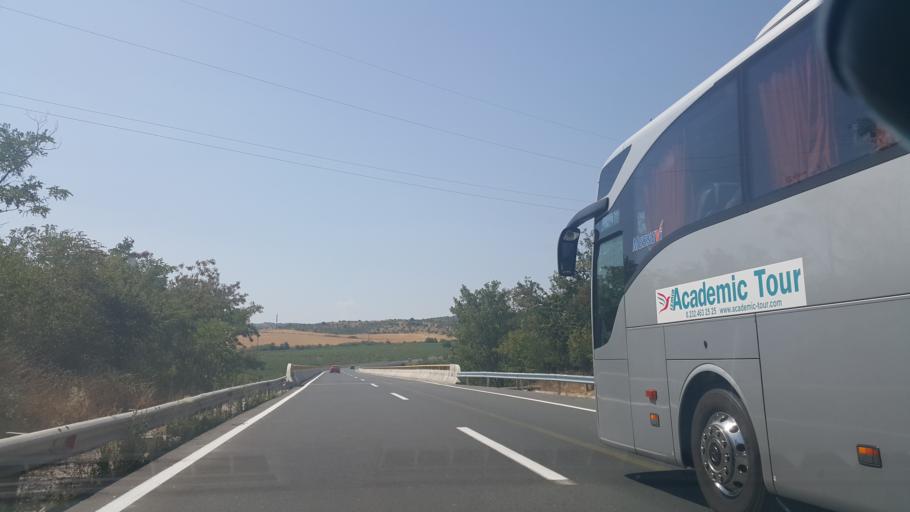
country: MK
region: Veles
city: Veles
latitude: 41.7830
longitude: 21.7608
